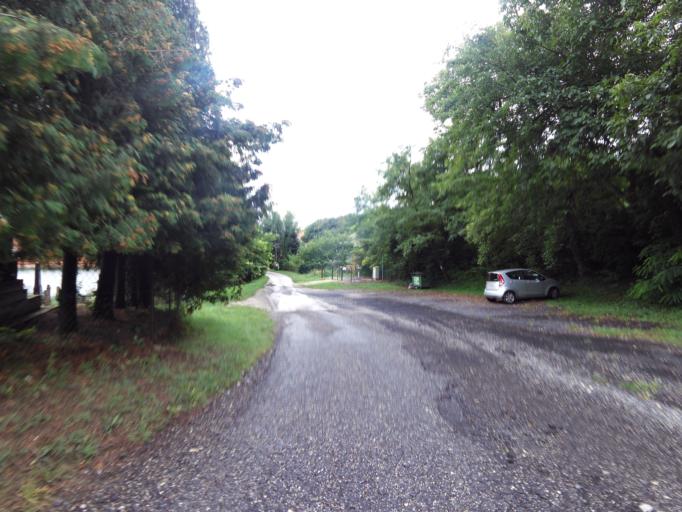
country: HU
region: Zala
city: Vonyarcvashegy
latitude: 46.8278
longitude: 17.3680
